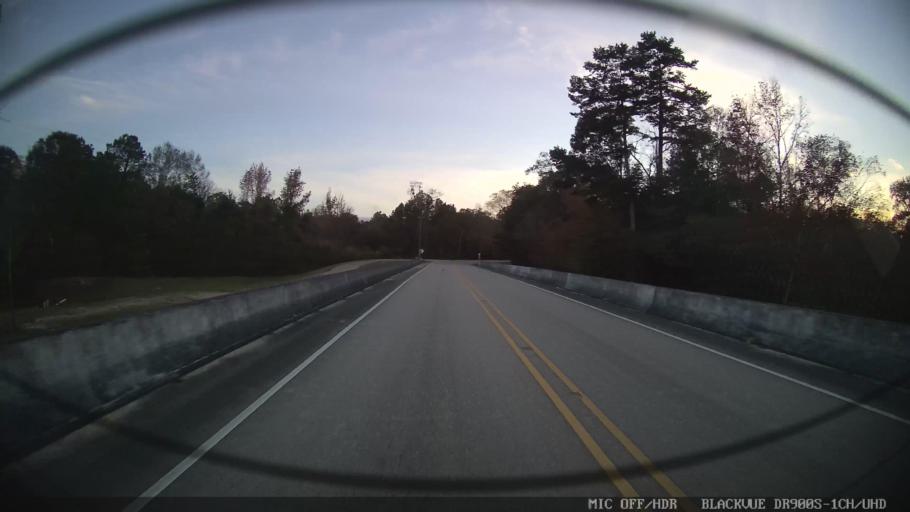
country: US
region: Mississippi
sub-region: Stone County
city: Wiggins
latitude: 31.0534
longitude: -89.1915
